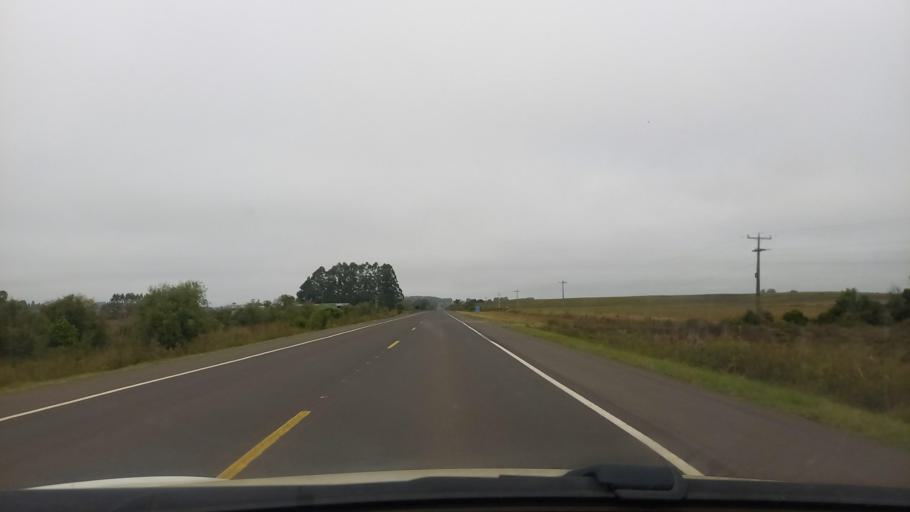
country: BR
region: Rio Grande do Sul
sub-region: Rosario Do Sul
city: Rosario do Sul
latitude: -30.3008
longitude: -54.9911
